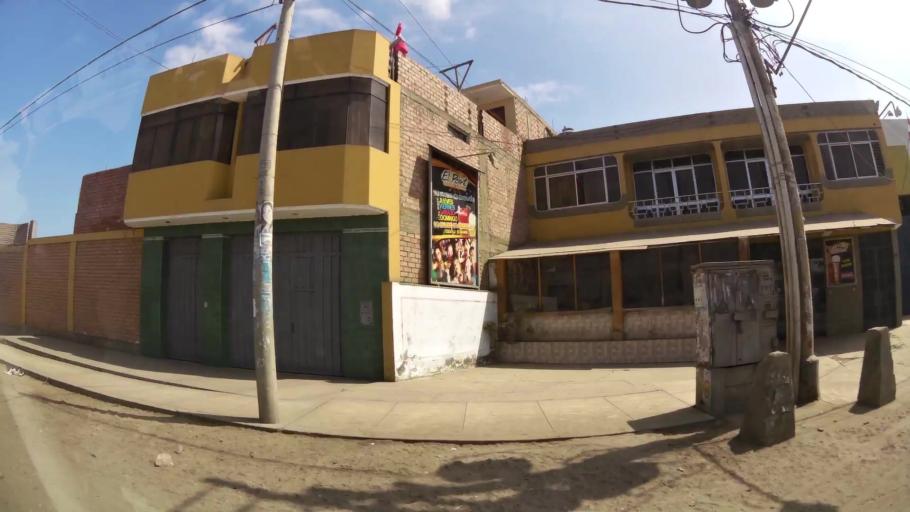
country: PE
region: Lima
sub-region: Provincia de Canete
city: Mala
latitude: -12.6593
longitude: -76.6375
